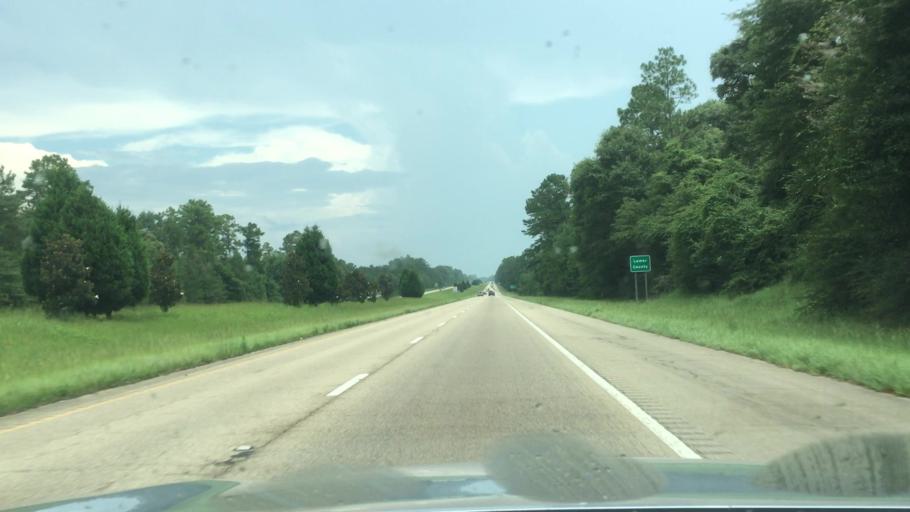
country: US
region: Mississippi
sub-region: Lamar County
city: Lumberton
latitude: 31.0096
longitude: -89.4141
